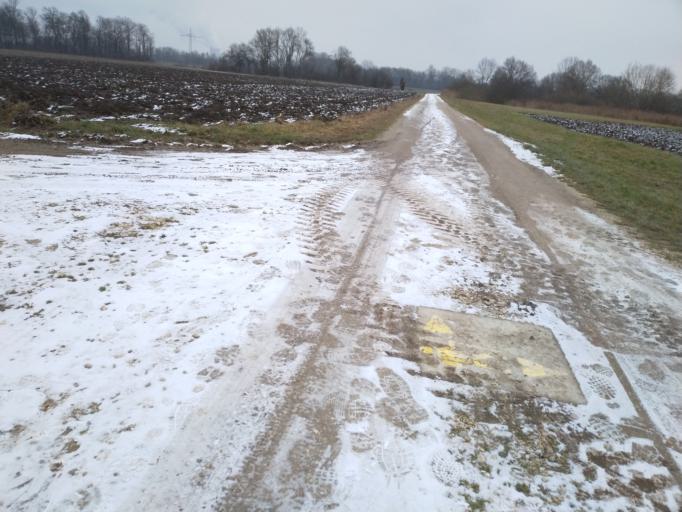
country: DE
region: Bavaria
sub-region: Swabia
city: Offingen
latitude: 48.4938
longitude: 10.3445
